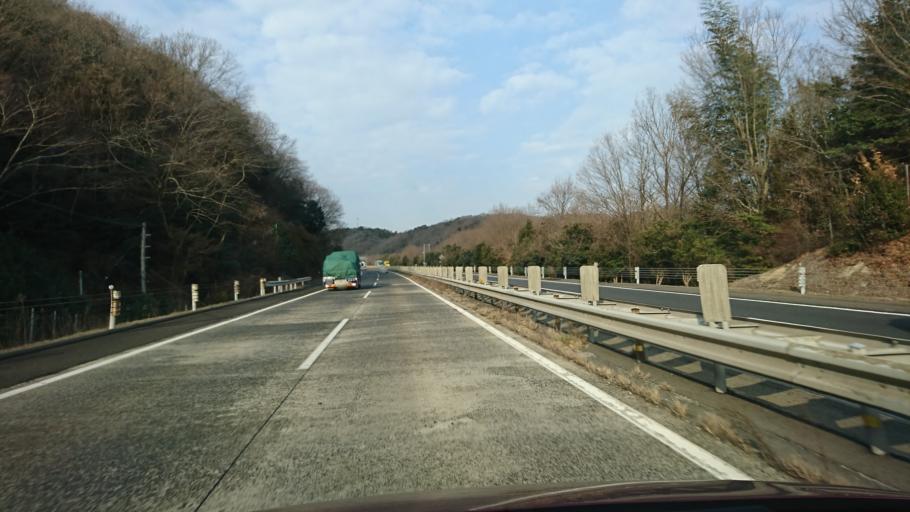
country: JP
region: Hyogo
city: Kariya
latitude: 34.7826
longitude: 134.2844
